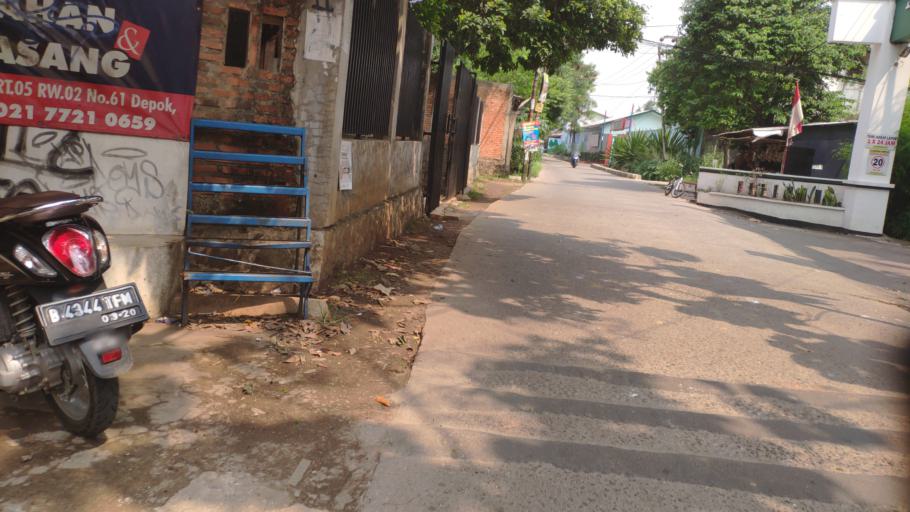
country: ID
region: West Java
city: Depok
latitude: -6.3809
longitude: 106.8021
